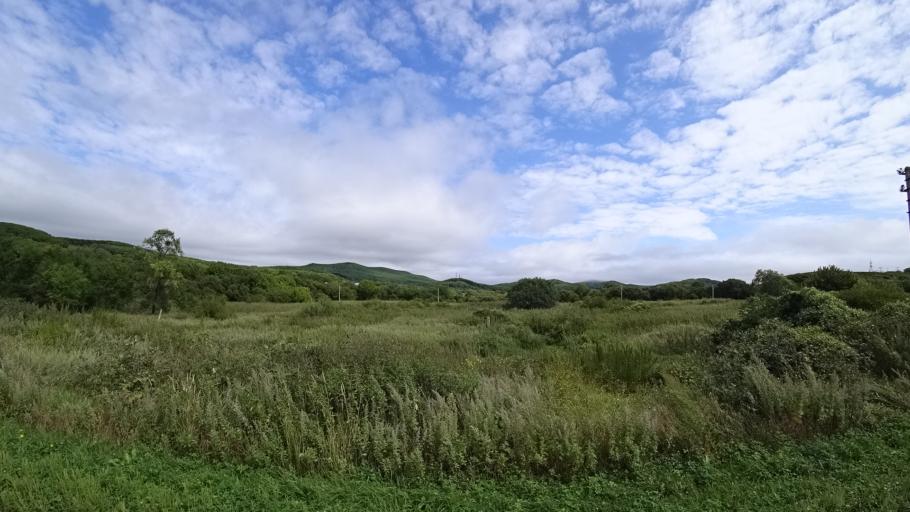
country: RU
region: Primorskiy
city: Lyalichi
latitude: 44.1349
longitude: 132.3879
